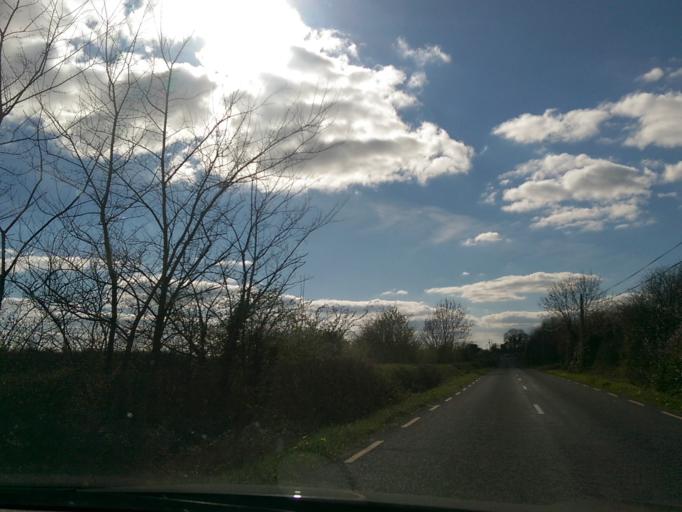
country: IE
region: Leinster
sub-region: Uibh Fhaili
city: Birr
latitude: 53.0942
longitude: -7.8675
